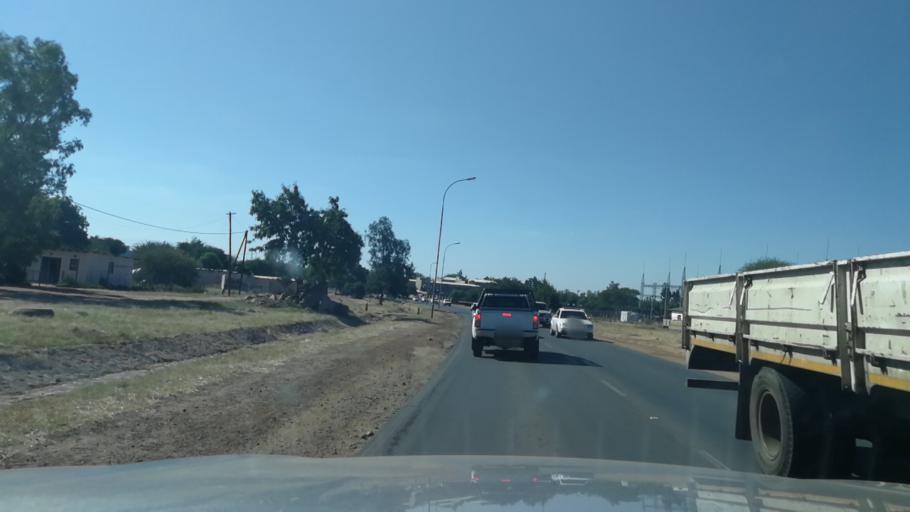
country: BW
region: South East
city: Gaborone
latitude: -24.6870
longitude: 25.9043
